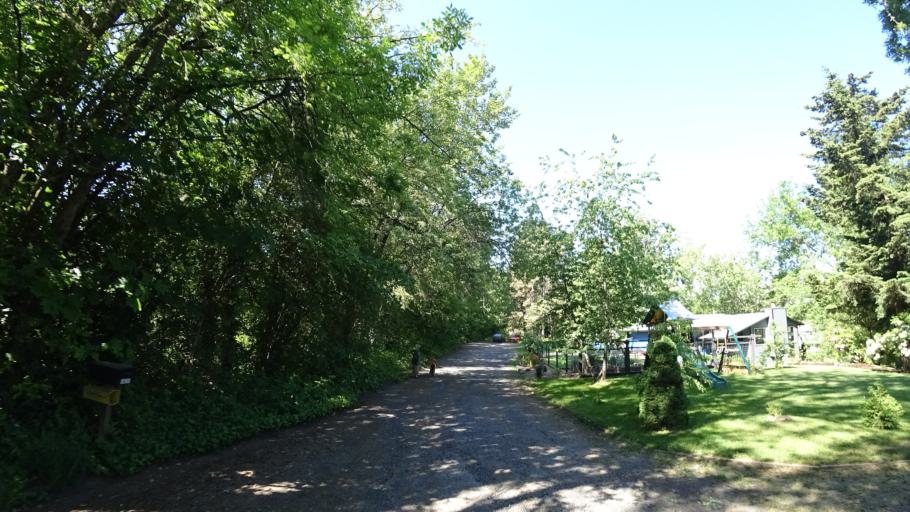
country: US
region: Oregon
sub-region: Washington County
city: Raleigh Hills
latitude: 45.4819
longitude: -122.7287
